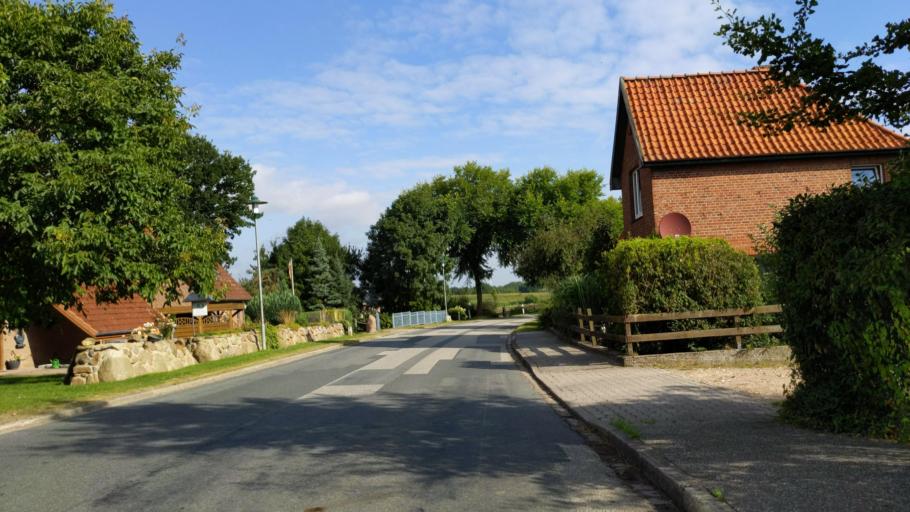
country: DE
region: Schleswig-Holstein
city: Bad Schwartau
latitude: 53.9680
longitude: 10.6552
